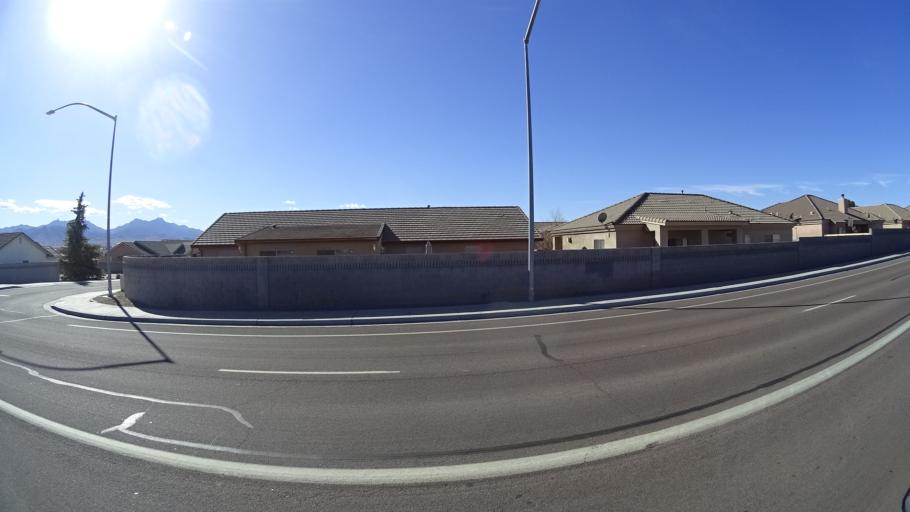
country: US
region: Arizona
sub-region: Mohave County
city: New Kingman-Butler
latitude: 35.2394
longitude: -114.0287
